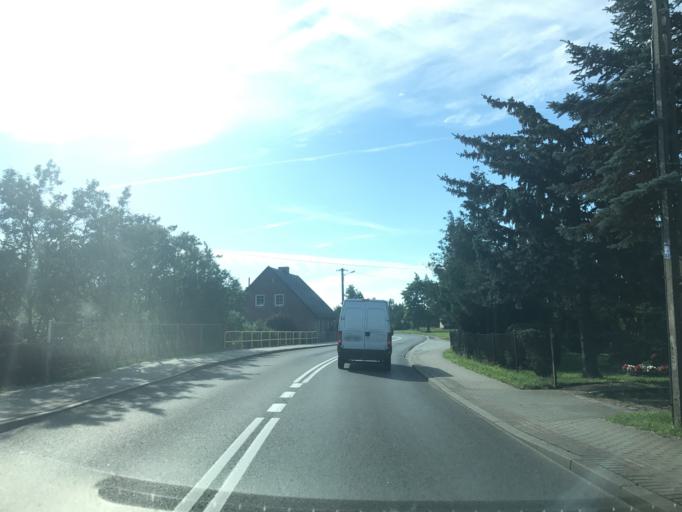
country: PL
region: Pomeranian Voivodeship
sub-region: Powiat czluchowski
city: Przechlewo
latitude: 53.7355
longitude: 17.1948
